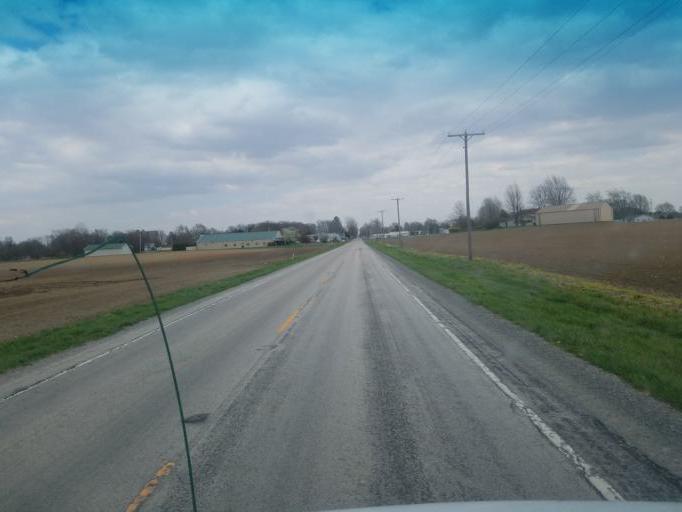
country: US
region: Ohio
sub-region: Wyandot County
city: Upper Sandusky
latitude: 40.9497
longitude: -83.1823
